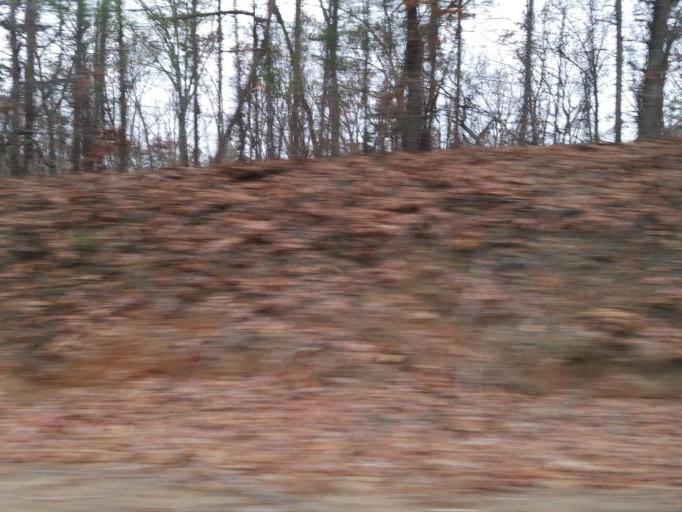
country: US
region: Georgia
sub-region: Dawson County
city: Dawsonville
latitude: 34.4295
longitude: -84.0544
